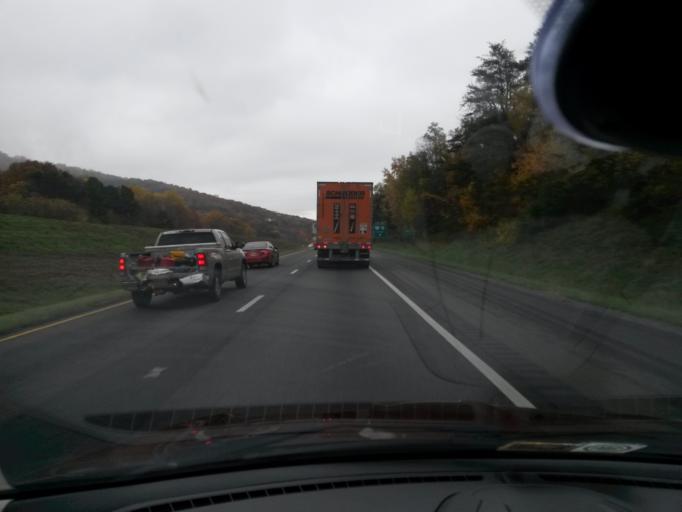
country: US
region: Virginia
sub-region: City of Salem
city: Salem
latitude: 37.2913
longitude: -80.1071
